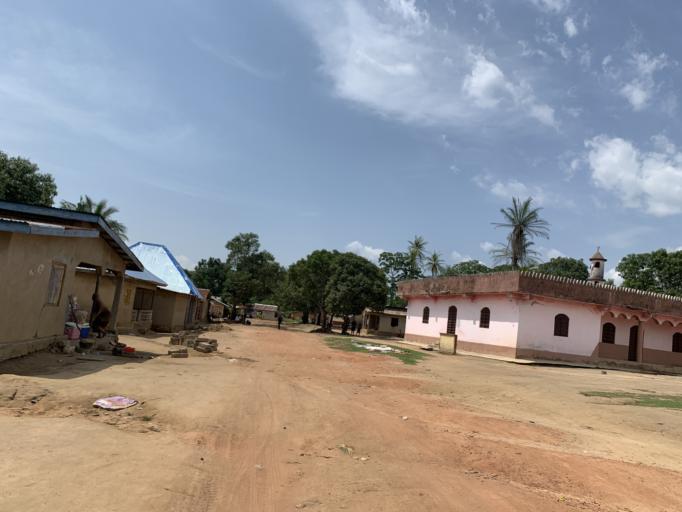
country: SL
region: Western Area
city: Waterloo
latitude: 8.3656
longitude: -13.0421
